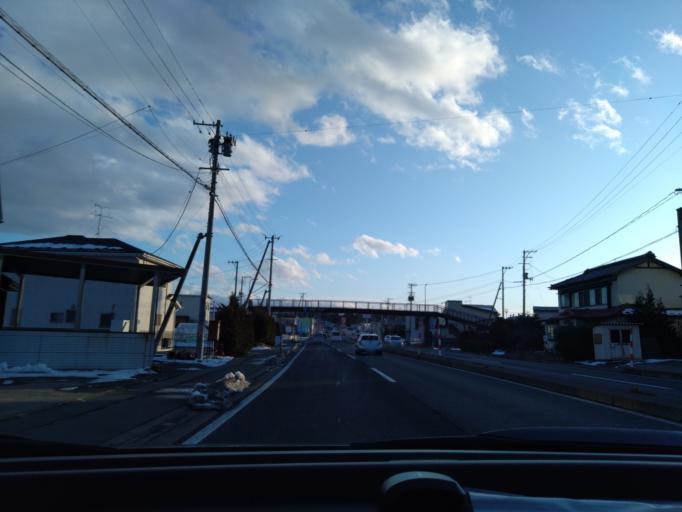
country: JP
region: Iwate
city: Morioka-shi
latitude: 39.5729
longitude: 141.1658
